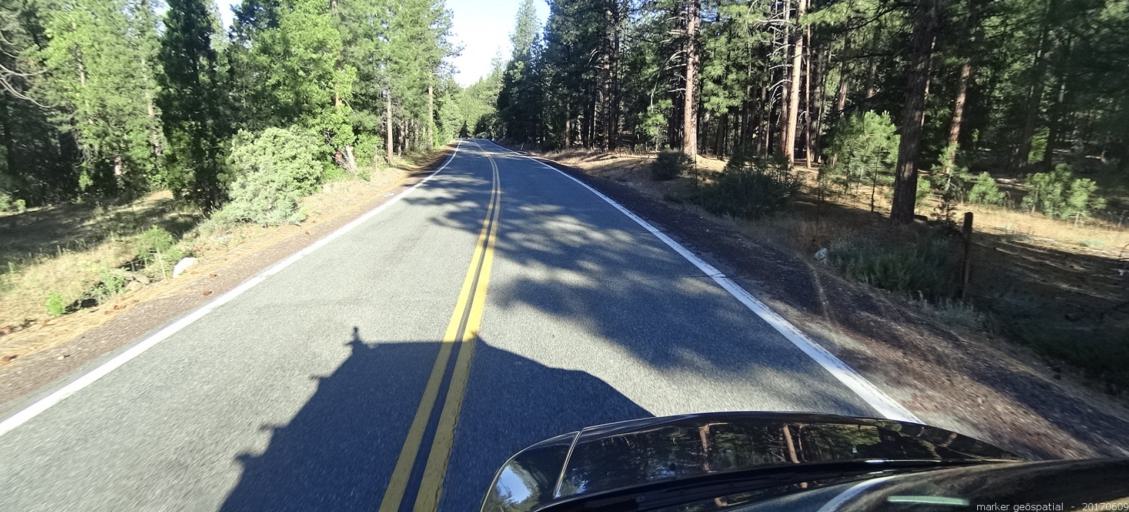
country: US
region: California
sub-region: Siskiyou County
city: Weed
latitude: 41.4024
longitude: -122.6493
